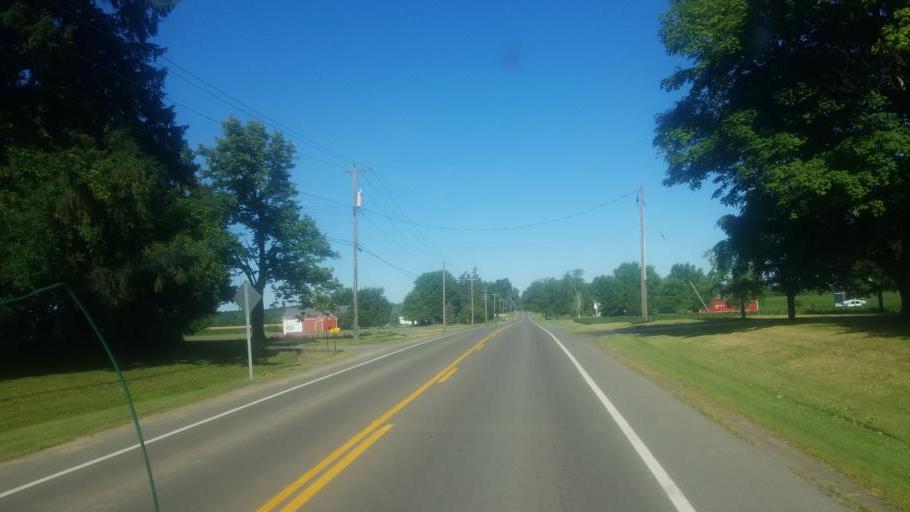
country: US
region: New York
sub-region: Ontario County
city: Phelps
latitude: 42.8861
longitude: -77.0815
